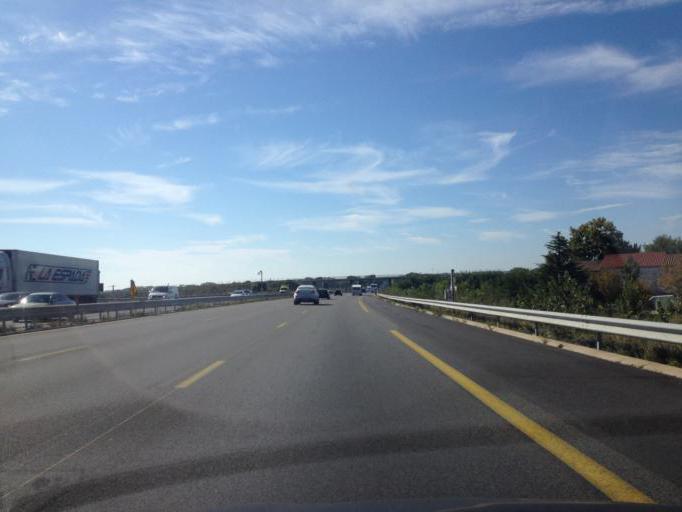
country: FR
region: Languedoc-Roussillon
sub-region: Departement de l'Herault
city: Saint-Aunes
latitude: 43.6334
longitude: 3.9695
